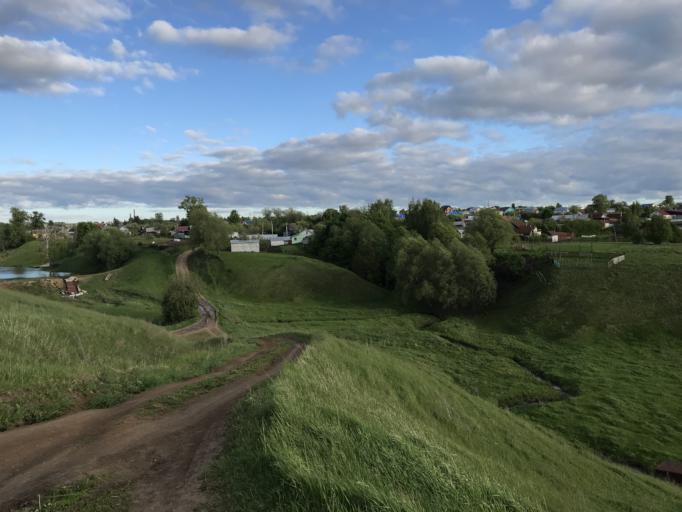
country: RU
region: Chuvashia
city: Kanash
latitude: 55.5407
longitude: 47.4976
